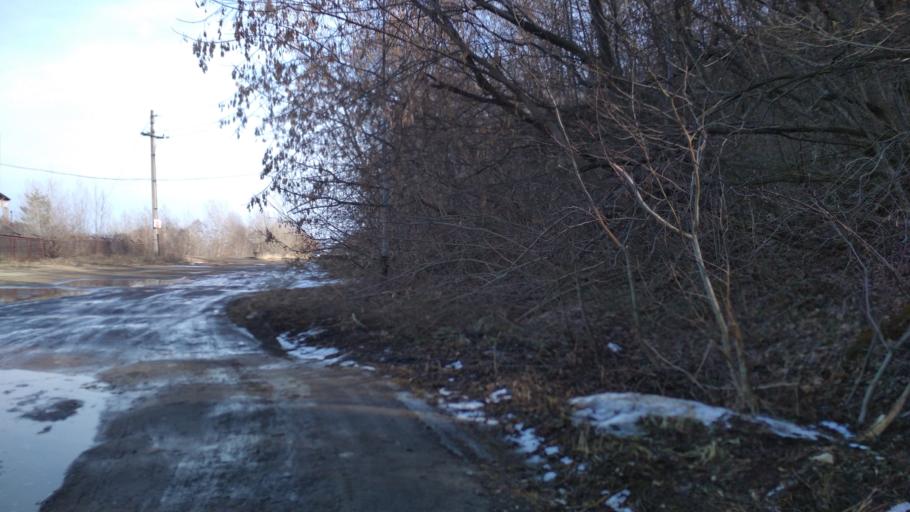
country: RU
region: Chuvashia
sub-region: Cheboksarskiy Rayon
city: Cheboksary
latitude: 56.1471
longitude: 47.3027
